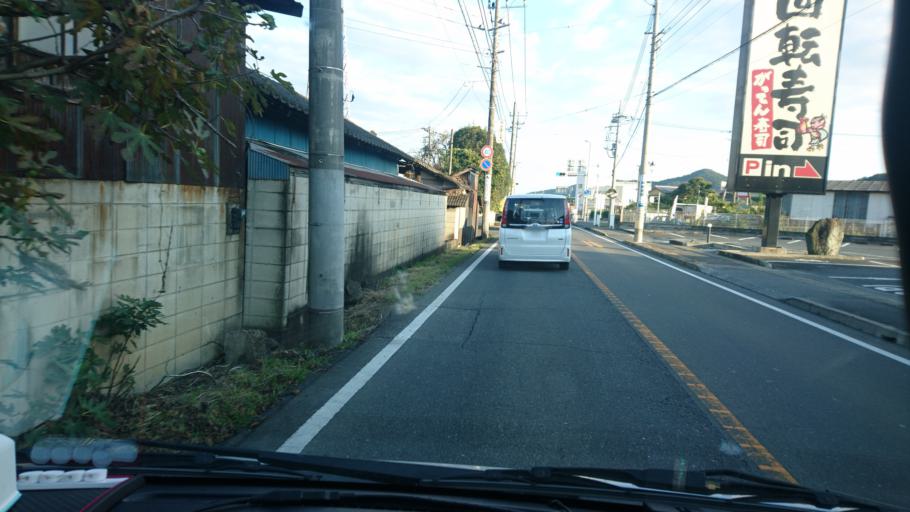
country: JP
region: Gunma
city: Kiryu
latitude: 36.3877
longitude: 139.3339
